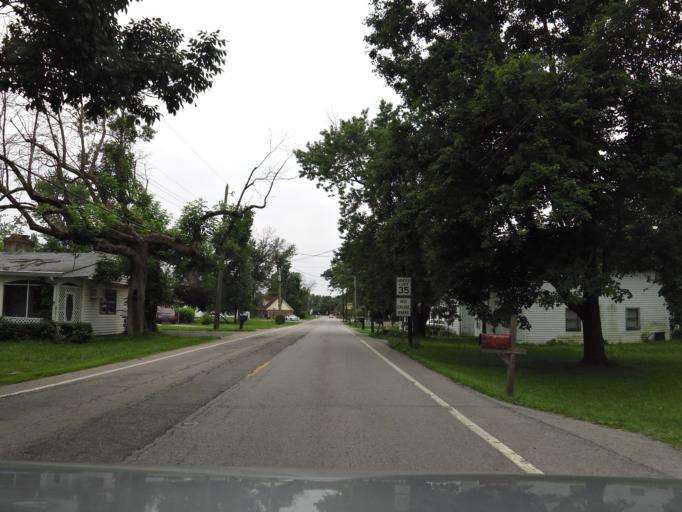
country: US
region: Ohio
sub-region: Clinton County
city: Blanchester
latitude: 39.3090
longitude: -83.9093
